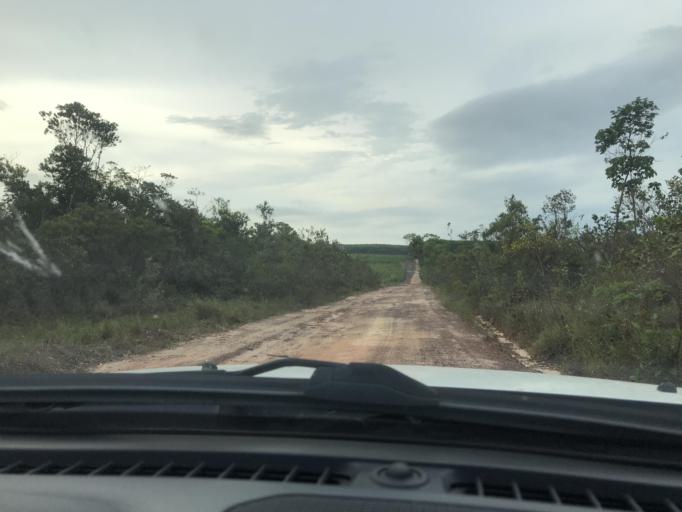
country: BR
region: Bahia
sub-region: Entre Rios
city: Entre Rios
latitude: -12.0882
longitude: -38.2026
